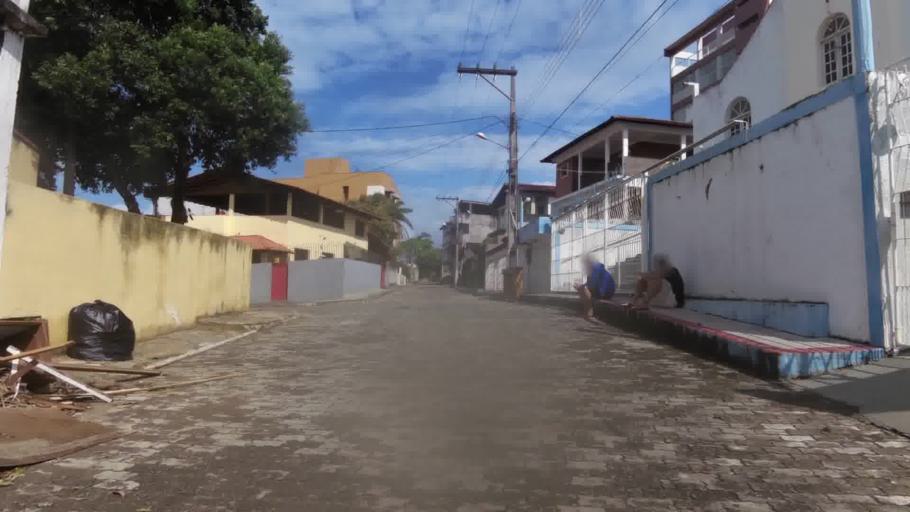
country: BR
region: Espirito Santo
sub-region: Piuma
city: Piuma
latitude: -20.8314
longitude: -40.6972
